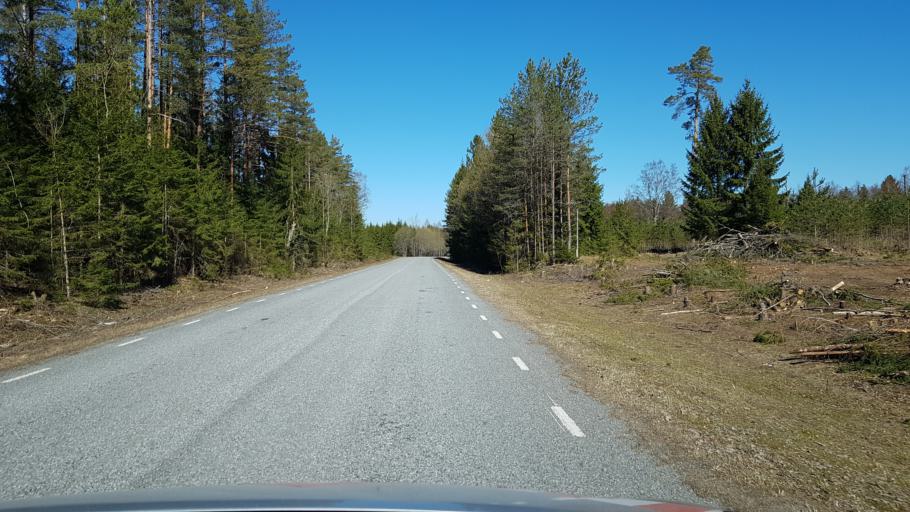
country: EE
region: Laeaene-Virumaa
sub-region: Haljala vald
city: Haljala
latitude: 59.4971
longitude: 26.2420
